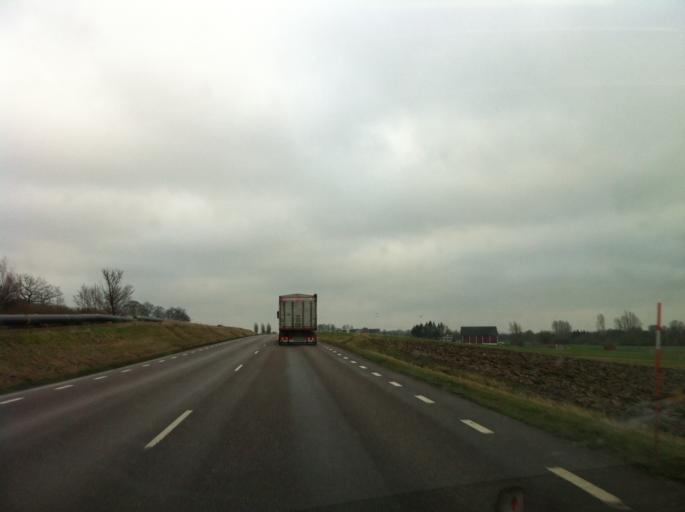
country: SE
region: Skane
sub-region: Kavlinge Kommun
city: Kaevlinge
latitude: 55.7966
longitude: 13.1647
